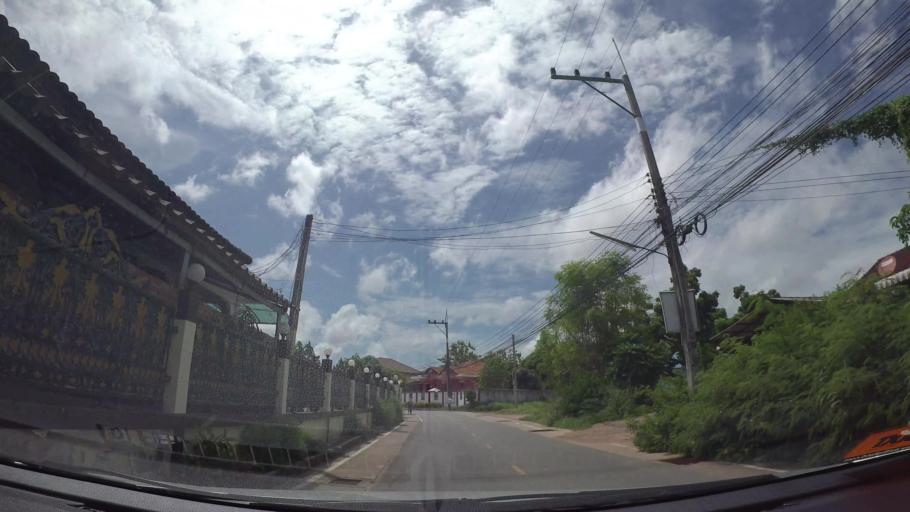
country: TH
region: Chon Buri
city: Sattahip
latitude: 12.6831
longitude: 100.9058
